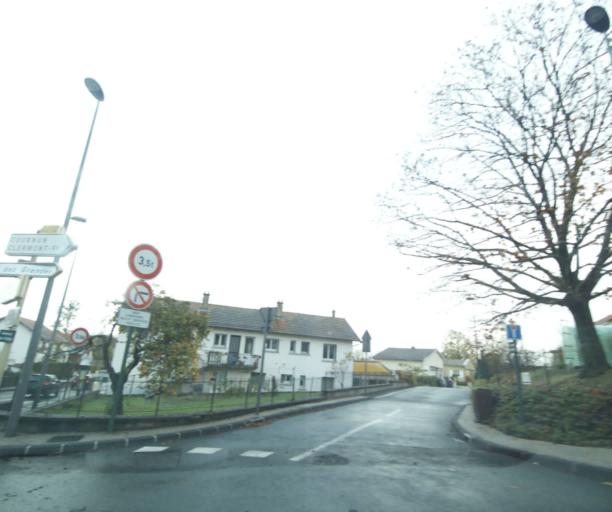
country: FR
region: Auvergne
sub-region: Departement du Puy-de-Dome
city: Le Cendre
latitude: 45.7244
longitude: 3.1919
